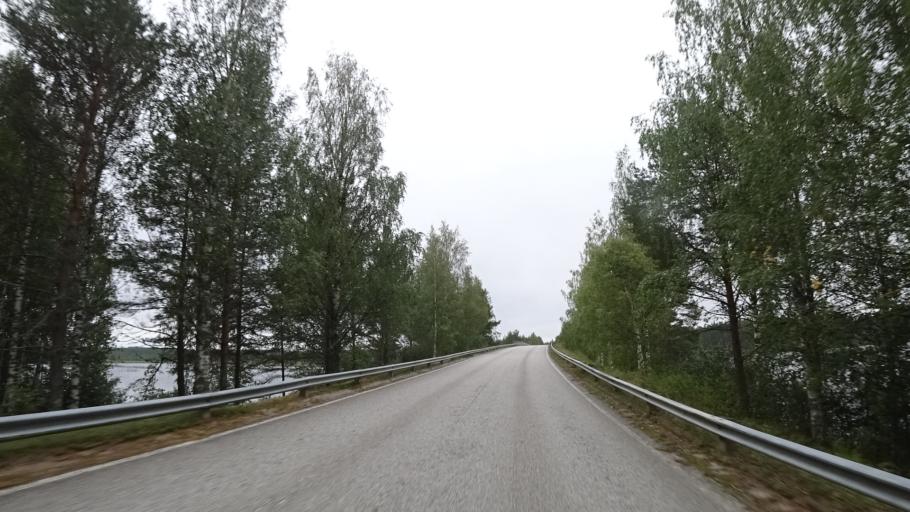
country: FI
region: North Karelia
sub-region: Pielisen Karjala
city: Lieksa
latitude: 63.3483
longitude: 30.2656
